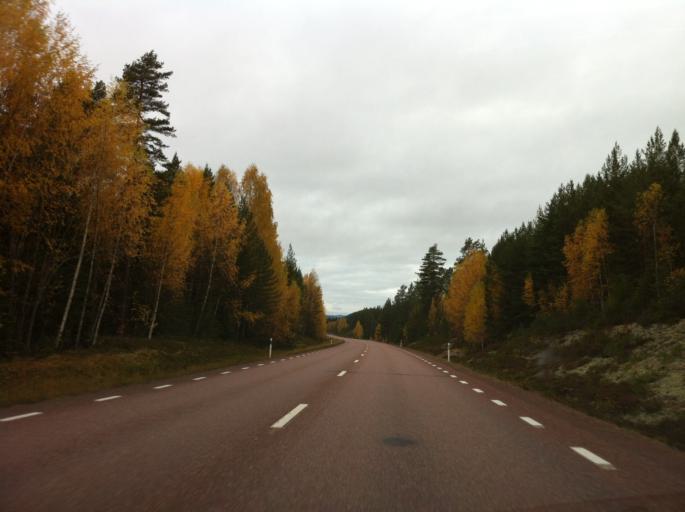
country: SE
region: Dalarna
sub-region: Mora Kommun
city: Mora
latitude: 61.0969
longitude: 14.2986
